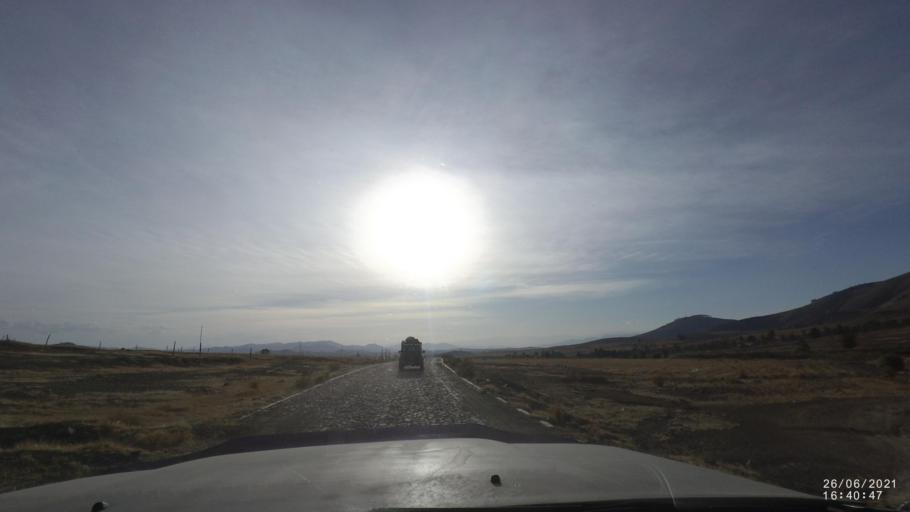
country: BO
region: Cochabamba
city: Arani
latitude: -17.7698
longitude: -65.8154
